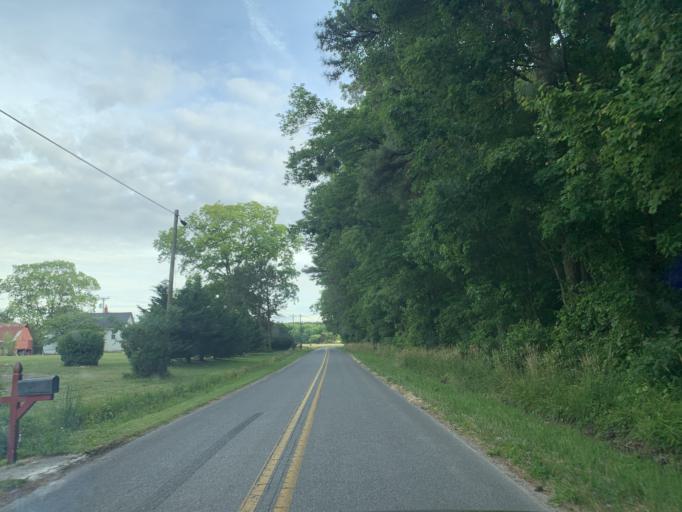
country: US
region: Maryland
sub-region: Worcester County
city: Pocomoke City
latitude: 38.0782
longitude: -75.4778
